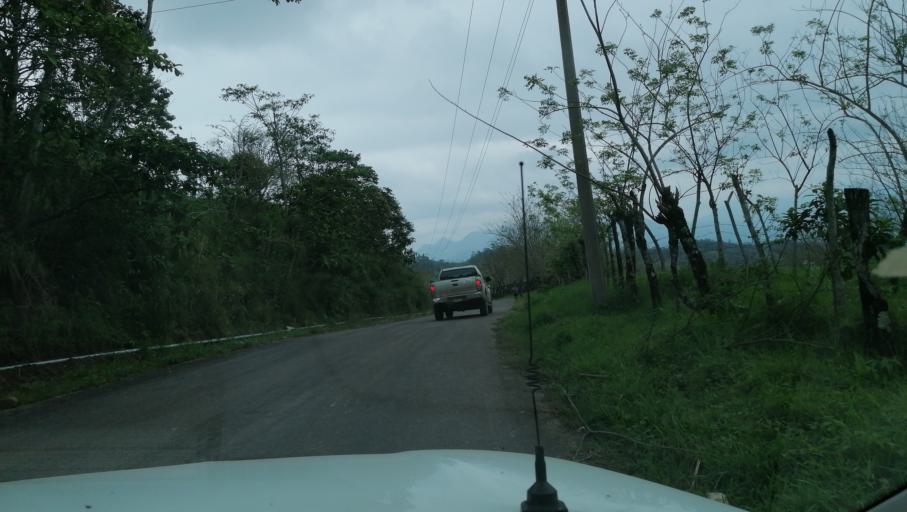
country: MX
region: Chiapas
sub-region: Francisco Leon
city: San Miguel la Sardina
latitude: 17.2763
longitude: -93.2719
